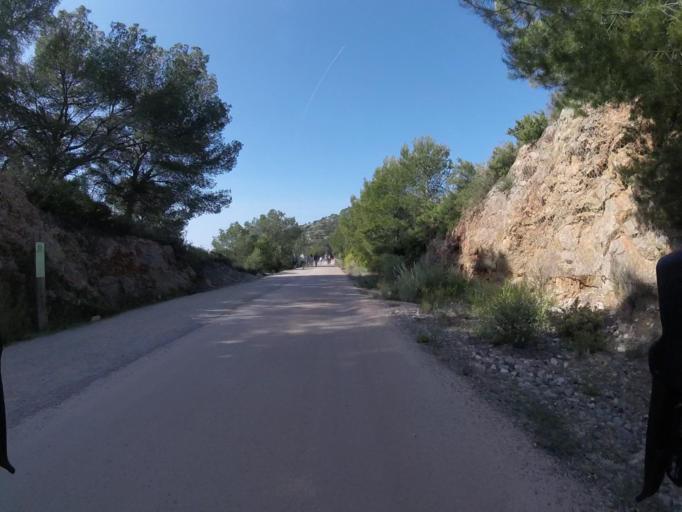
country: ES
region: Valencia
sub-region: Provincia de Castello
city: Orpesa/Oropesa del Mar
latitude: 40.0783
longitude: 0.1336
